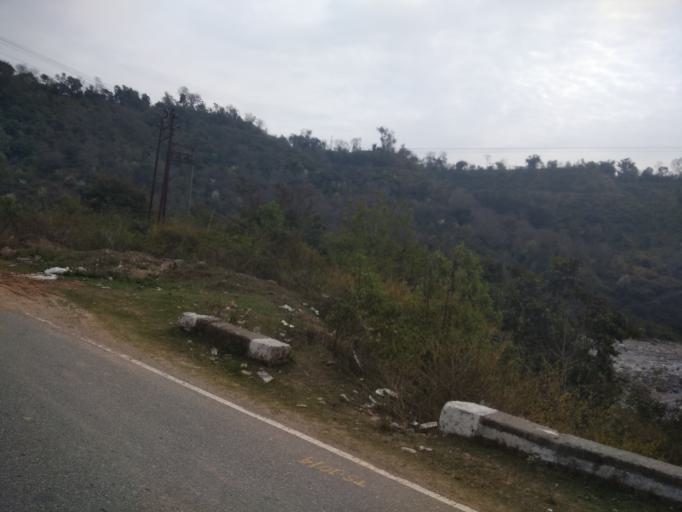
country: IN
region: Himachal Pradesh
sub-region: Kangra
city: Kotla
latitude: 32.2287
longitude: 76.0640
